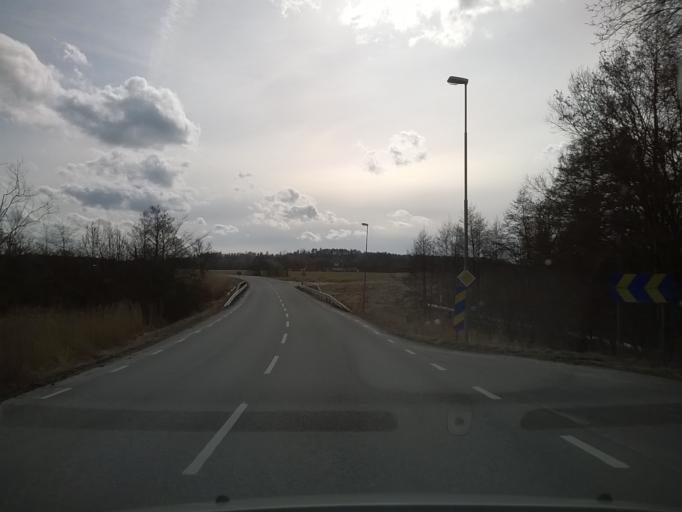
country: SE
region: Vaestra Goetaland
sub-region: Stenungsunds Kommun
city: Stora Hoga
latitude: 57.9823
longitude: 11.8252
